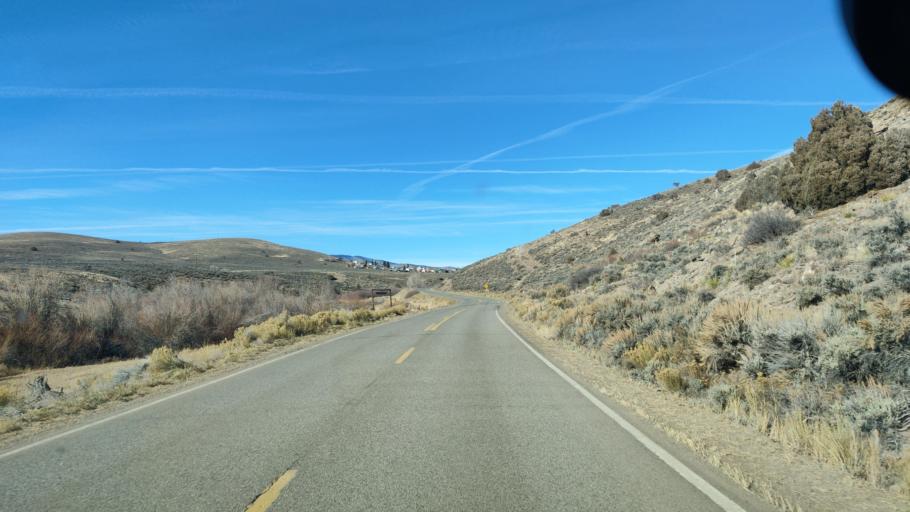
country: US
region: Colorado
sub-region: Gunnison County
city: Gunnison
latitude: 38.5663
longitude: -106.9583
